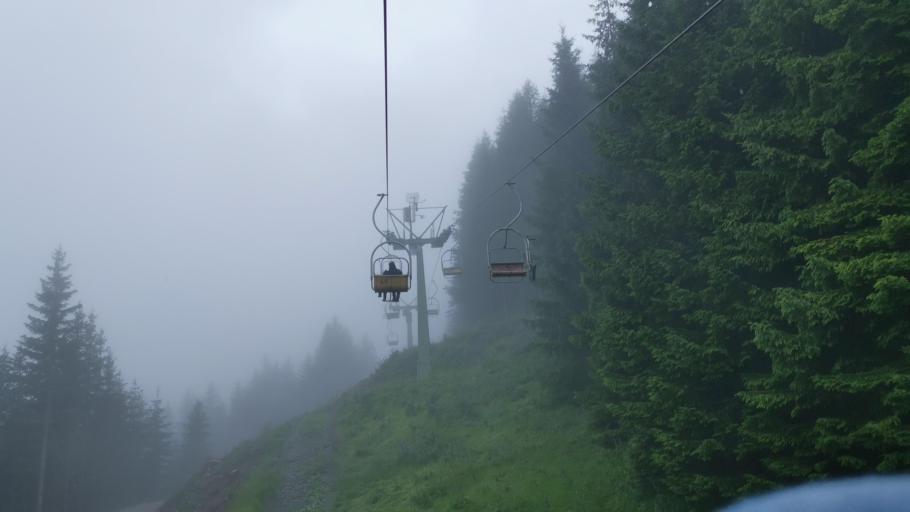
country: AT
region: Tyrol
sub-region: Politischer Bezirk Lienz
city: Leisach
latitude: 46.8193
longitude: 12.7299
